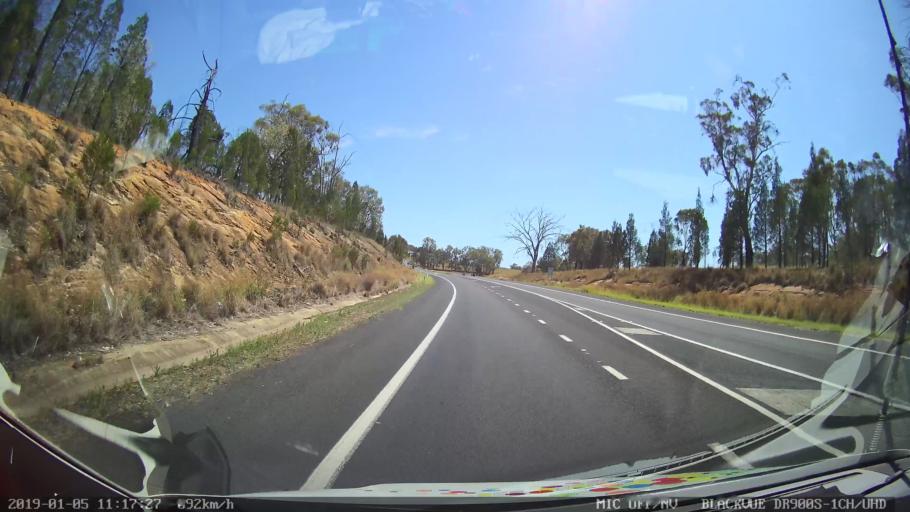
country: AU
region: New South Wales
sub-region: Warrumbungle Shire
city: Coonabarabran
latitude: -31.3266
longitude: 149.3072
